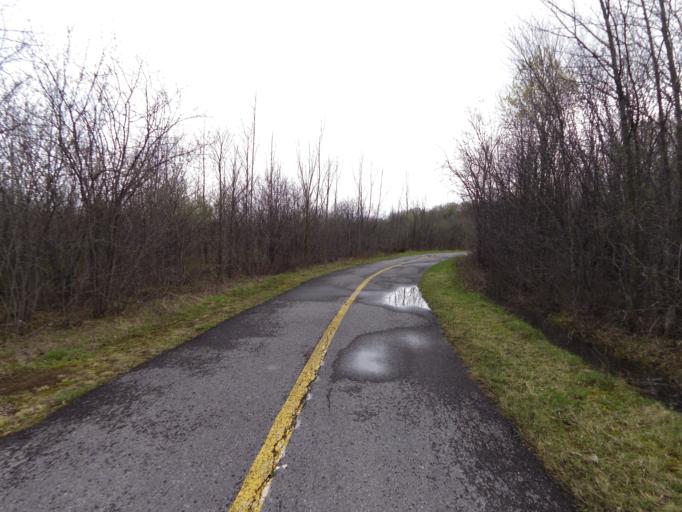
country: CA
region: Quebec
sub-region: Outaouais
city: Gatineau
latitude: 45.4686
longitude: -75.7791
